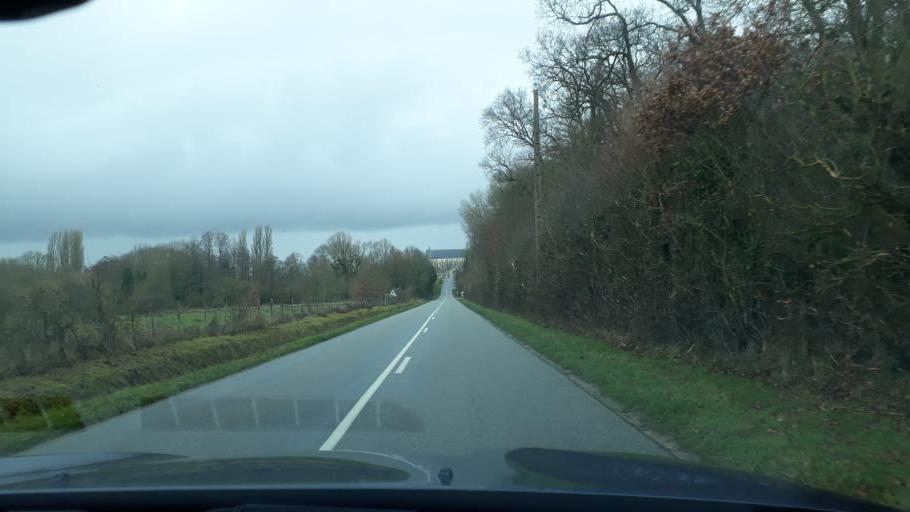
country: FR
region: Centre
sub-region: Departement du Loiret
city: Clery-Saint-Andre
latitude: 47.8135
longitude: 1.7601
